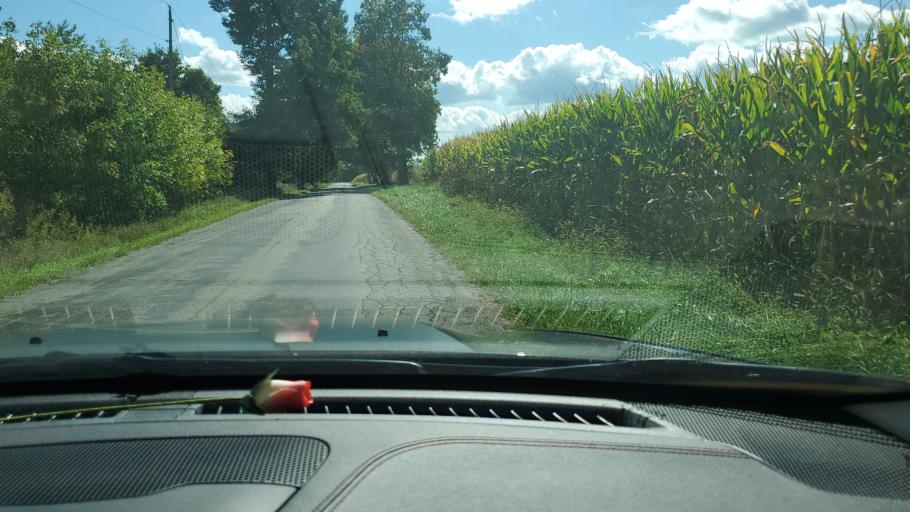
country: US
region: Ohio
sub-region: Ashtabula County
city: Andover
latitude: 41.4650
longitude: -80.5869
